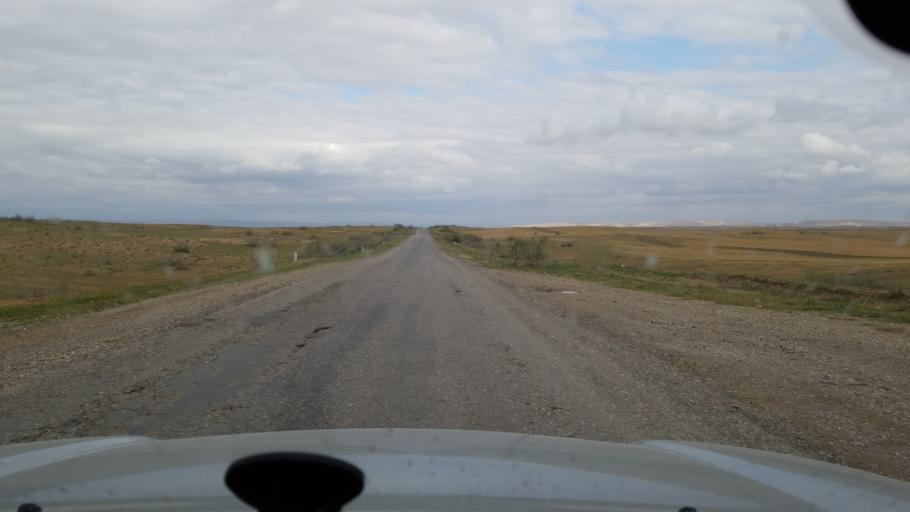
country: TM
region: Mary
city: Serhetabat
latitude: 35.9848
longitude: 62.6302
